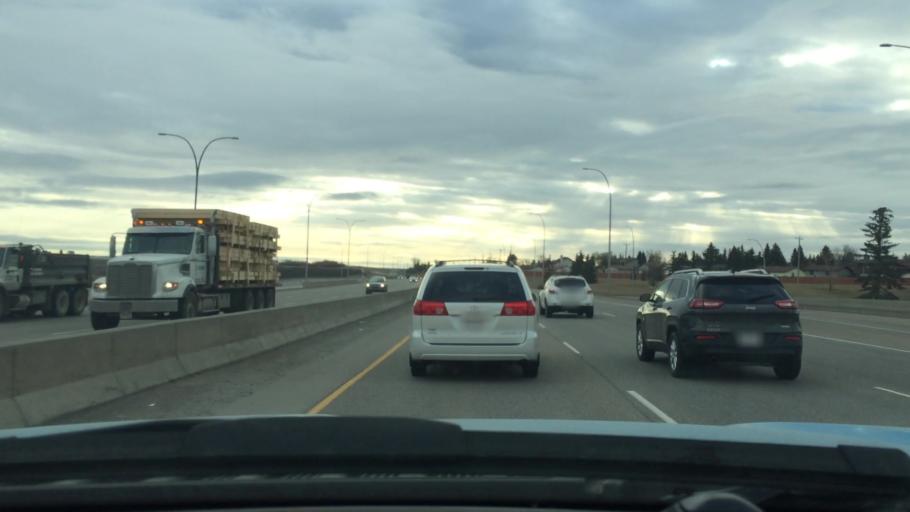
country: CA
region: Alberta
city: Calgary
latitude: 51.1340
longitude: -114.0710
